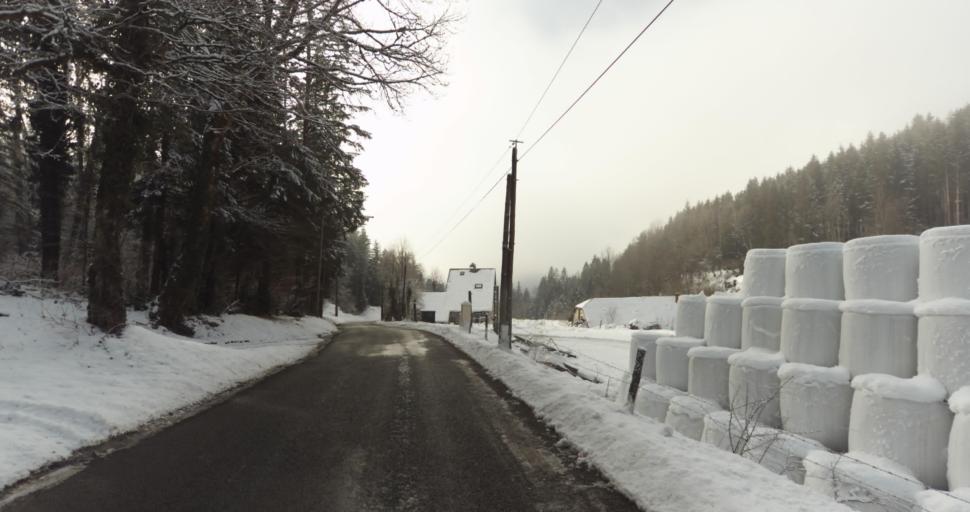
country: FR
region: Rhone-Alpes
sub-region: Departement de l'Ain
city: Nantua
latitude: 46.1581
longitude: 5.6275
